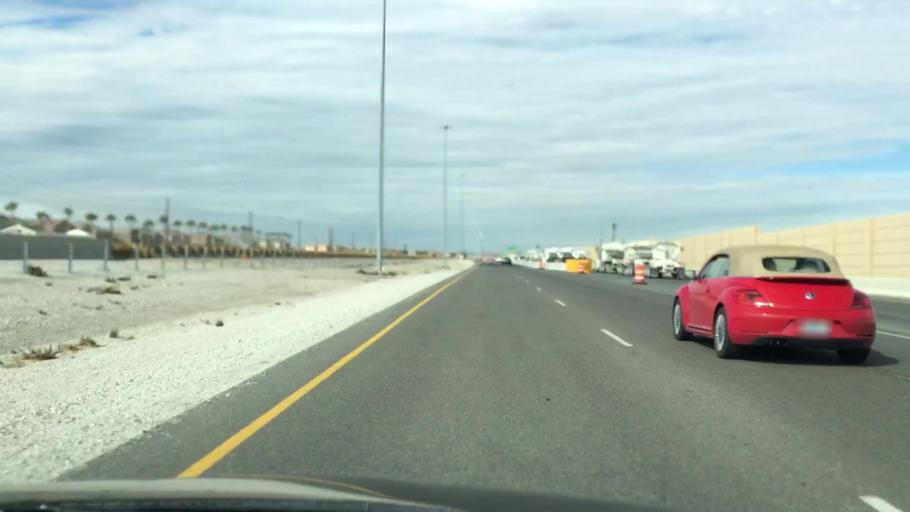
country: US
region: Nevada
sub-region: Clark County
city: Summerlin South
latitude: 36.3034
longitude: -115.2903
